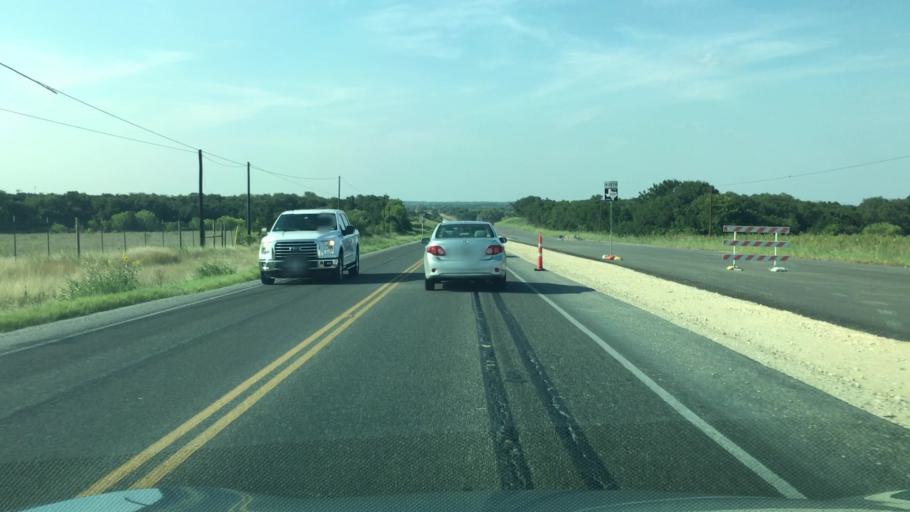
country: US
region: Texas
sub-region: Hays County
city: Buda
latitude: 30.0528
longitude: -97.8745
